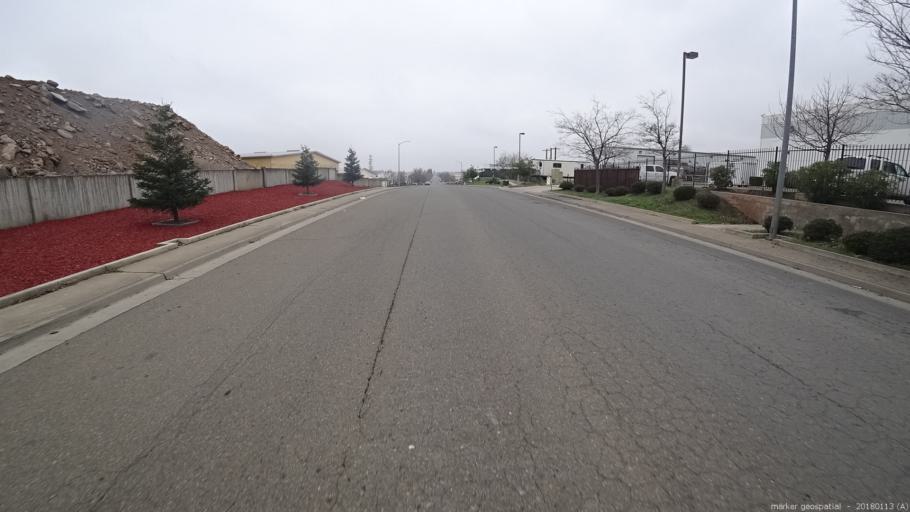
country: US
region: California
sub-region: Sacramento County
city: Gold River
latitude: 38.5795
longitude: -121.2551
